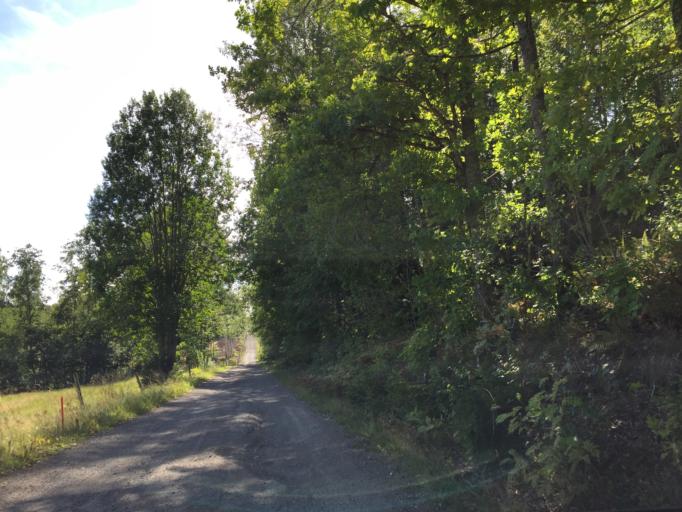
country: NO
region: Vestfold
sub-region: Hof
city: Hof
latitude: 59.4580
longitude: 10.1459
